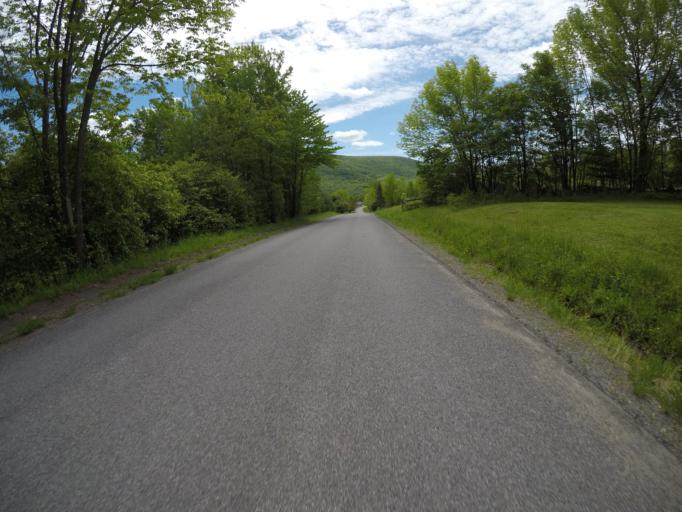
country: US
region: New York
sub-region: Delaware County
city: Stamford
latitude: 42.2719
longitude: -74.5196
